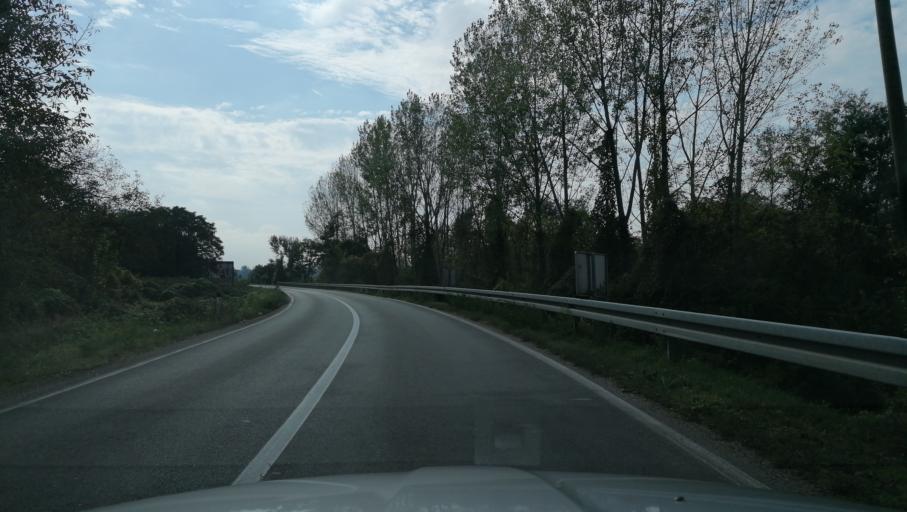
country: BA
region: Republika Srpska
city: Balatun
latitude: 44.8921
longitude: 19.3345
